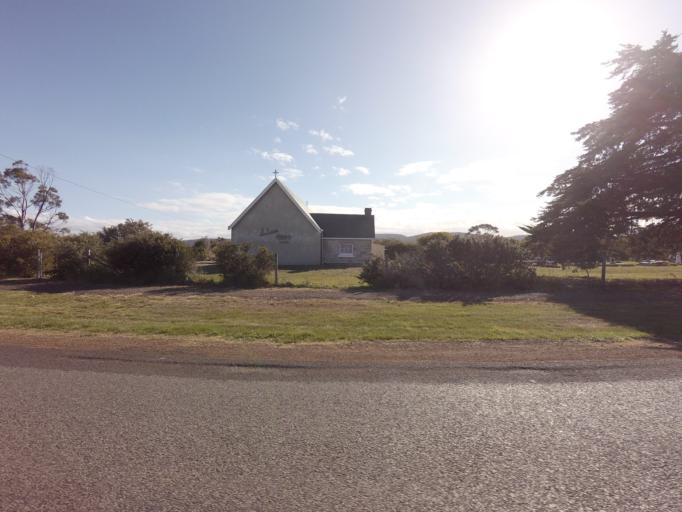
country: AU
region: Tasmania
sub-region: Sorell
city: Sorell
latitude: -42.5034
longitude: 147.9155
